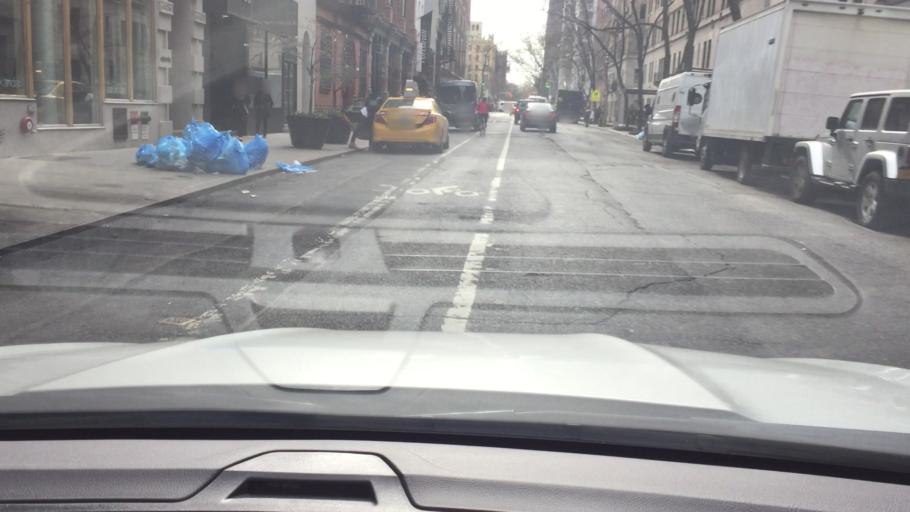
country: US
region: New York
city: New York City
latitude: 40.7324
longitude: -73.9932
